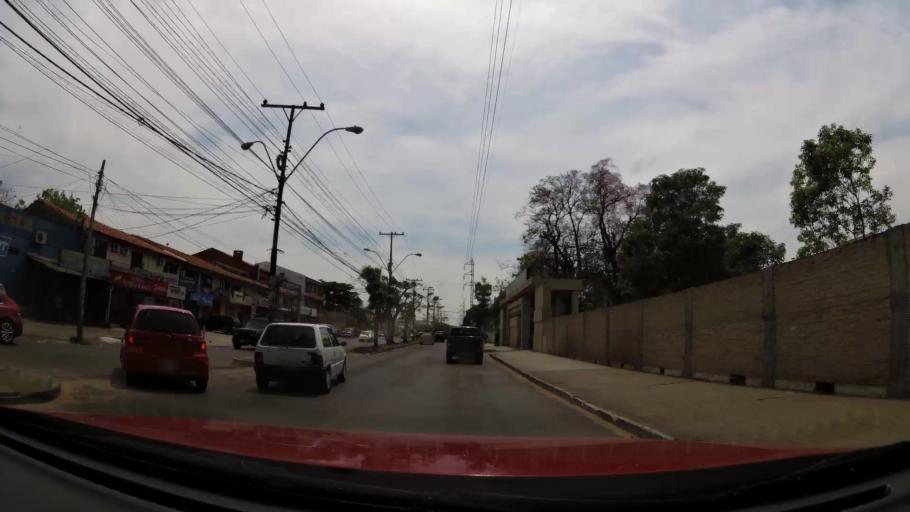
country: PY
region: Asuncion
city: Asuncion
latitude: -25.2576
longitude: -57.5857
